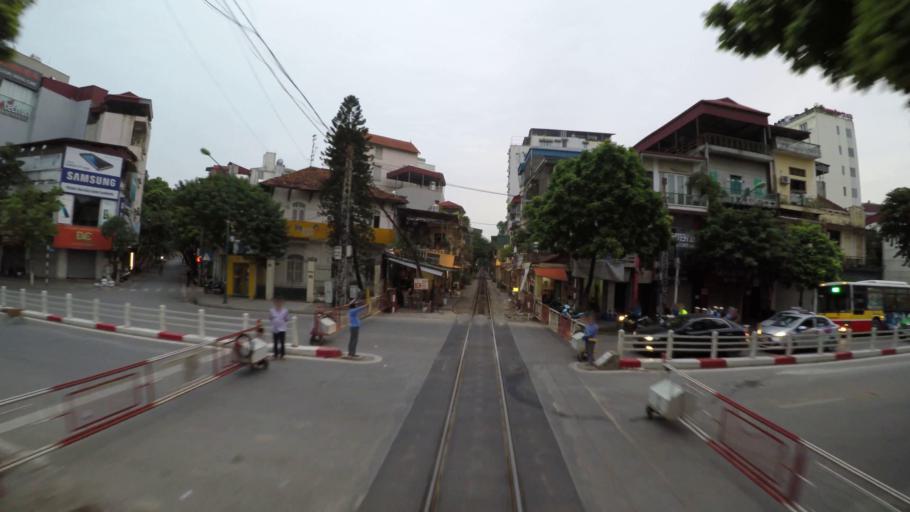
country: VN
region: Ha Noi
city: Hoan Kiem
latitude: 21.0368
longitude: 105.8461
